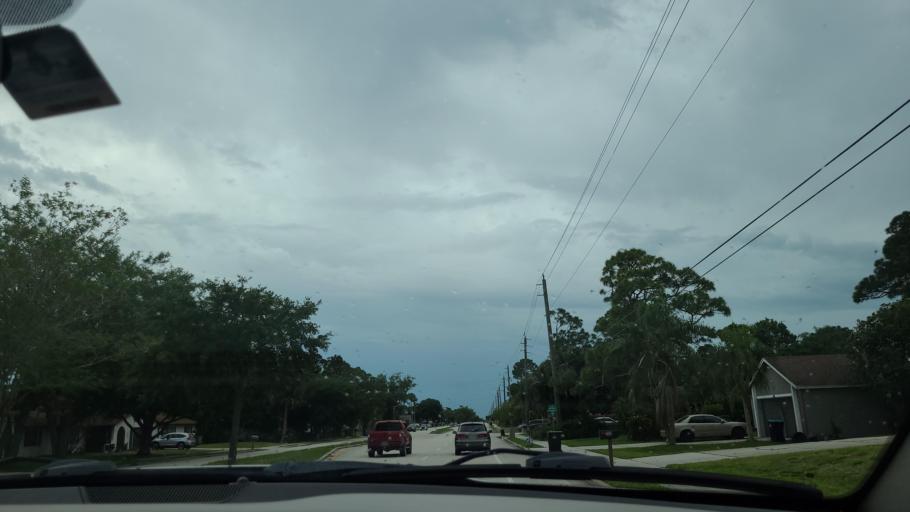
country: US
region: Florida
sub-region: Brevard County
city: Palm Bay
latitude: 27.9969
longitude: -80.6486
